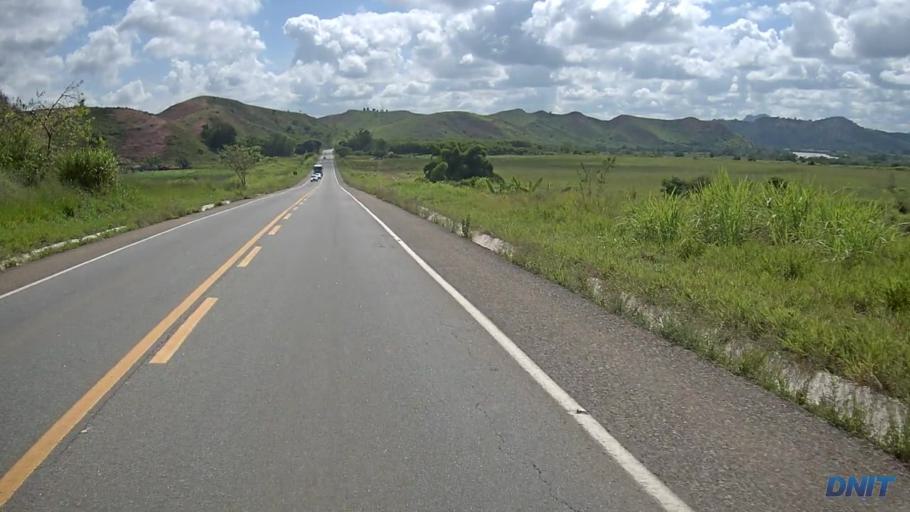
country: BR
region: Minas Gerais
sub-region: Belo Oriente
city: Belo Oriente
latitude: -19.1438
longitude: -42.2273
